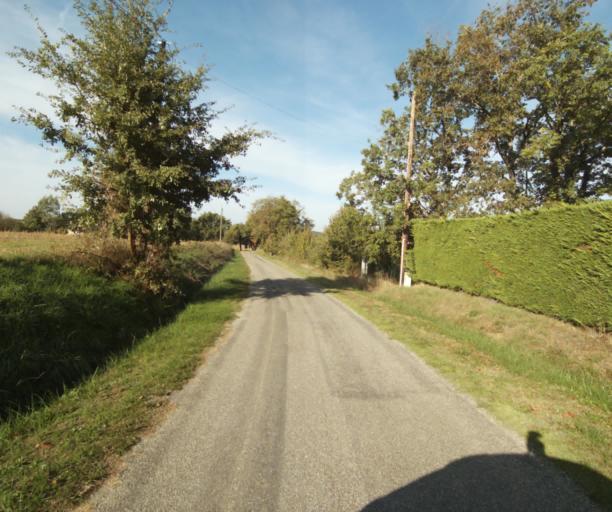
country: FR
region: Midi-Pyrenees
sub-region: Departement du Tarn-et-Garonne
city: Nohic
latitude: 43.9269
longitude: 1.4519
